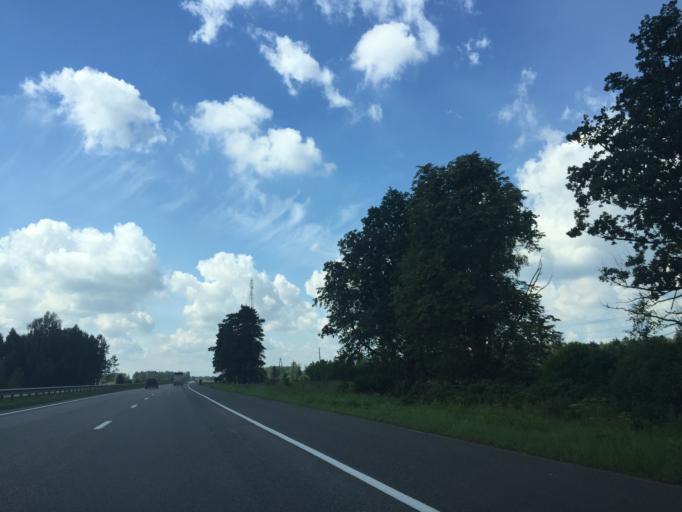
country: LV
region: Olaine
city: Olaine
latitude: 56.8197
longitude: 24.0172
